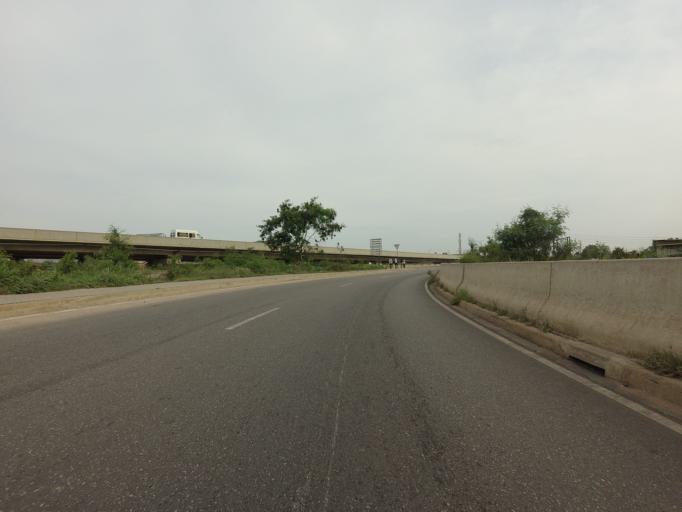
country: GH
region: Greater Accra
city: Gbawe
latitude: 5.5727
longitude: -0.2830
